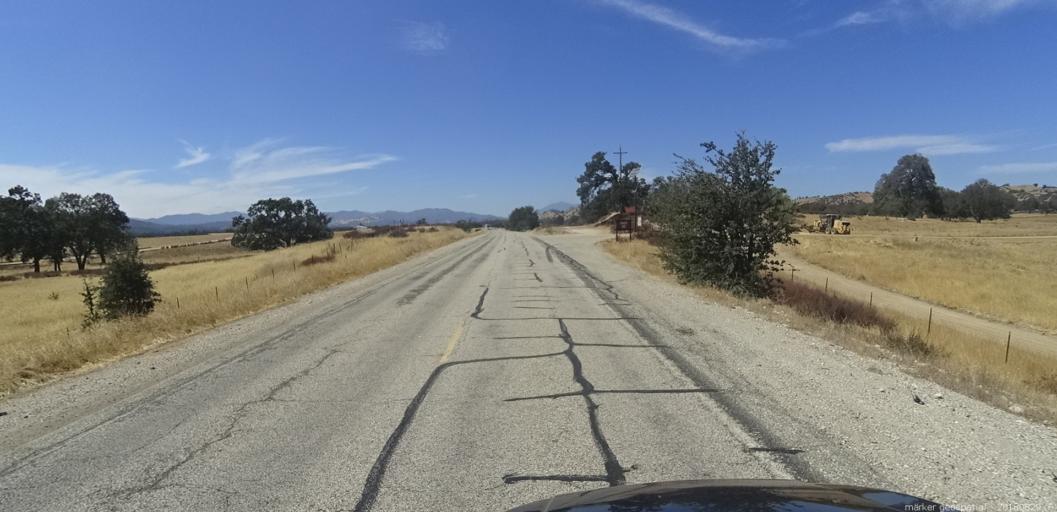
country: US
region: California
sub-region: Monterey County
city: King City
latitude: 35.9583
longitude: -121.1578
